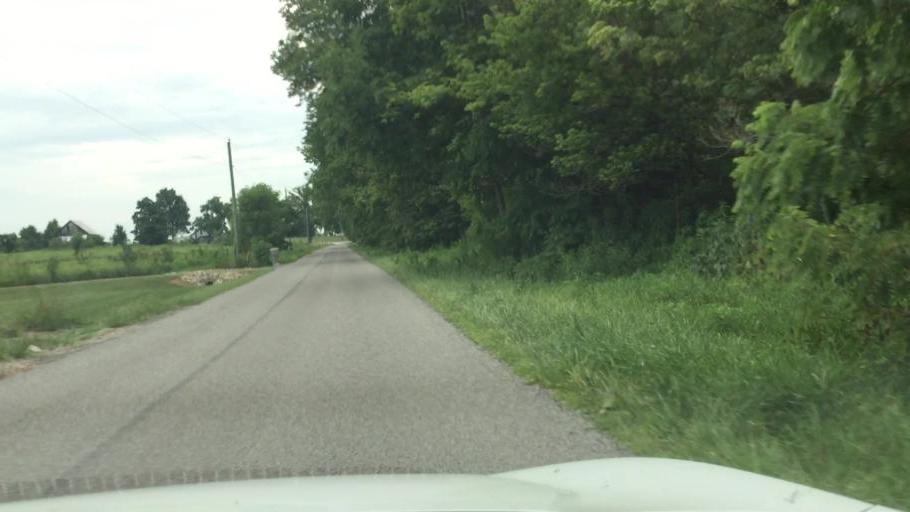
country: US
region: Ohio
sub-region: Champaign County
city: North Lewisburg
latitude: 40.2443
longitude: -83.5230
